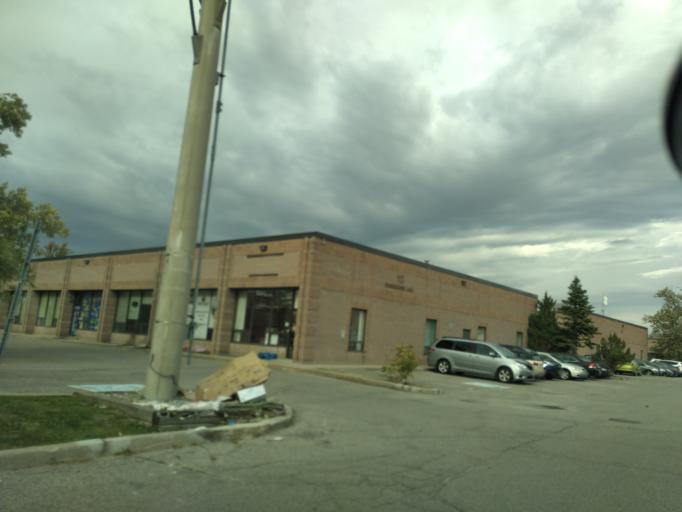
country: CA
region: Ontario
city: Newmarket
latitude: 43.9886
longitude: -79.4499
